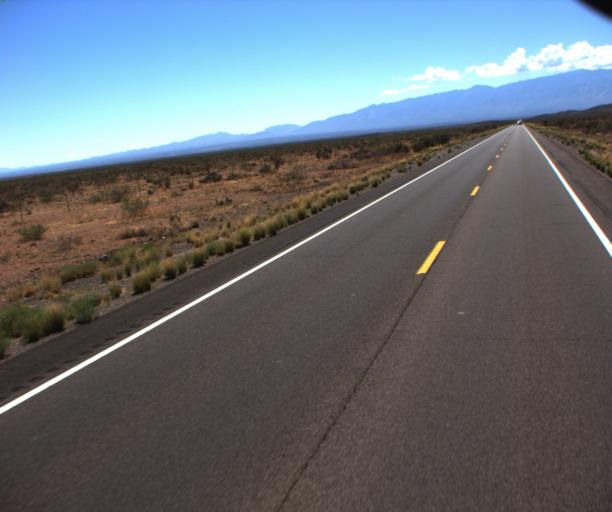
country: US
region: Arizona
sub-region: Graham County
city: Safford
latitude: 32.8199
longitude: -109.4783
